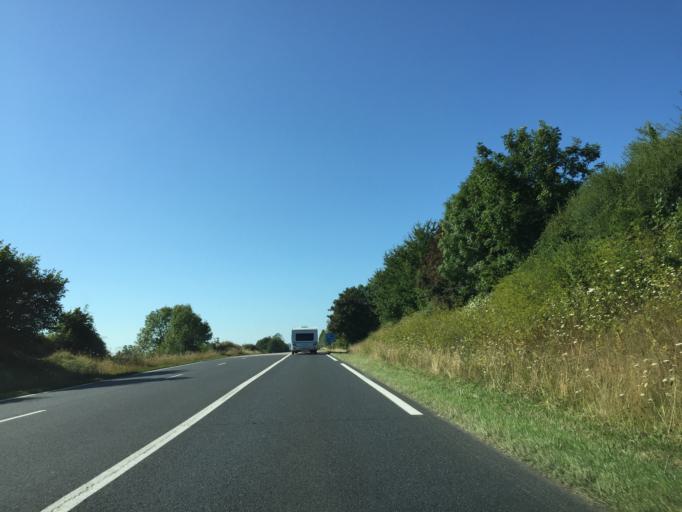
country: FR
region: Lower Normandy
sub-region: Departement du Calvados
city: Saint-Gatien-des-Bois
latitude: 49.2827
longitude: 0.2124
